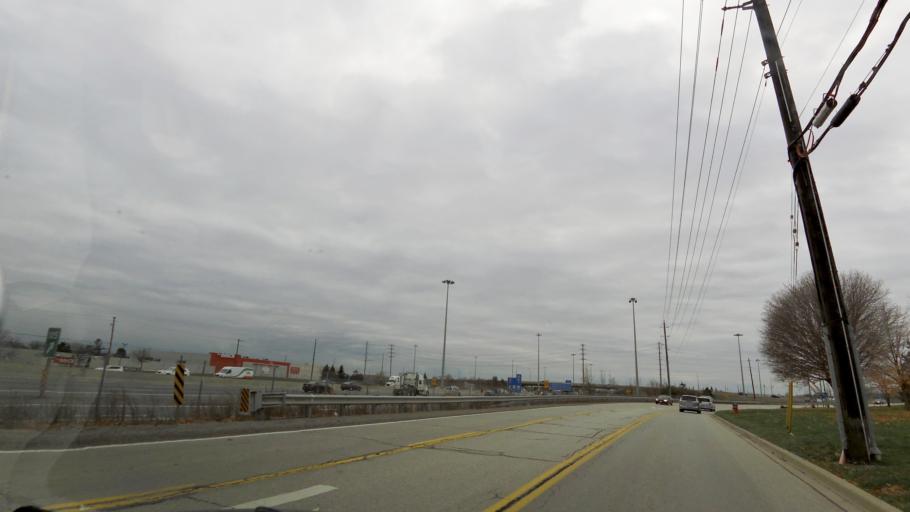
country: CA
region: Ontario
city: Burlington
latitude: 43.3691
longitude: -79.7859
